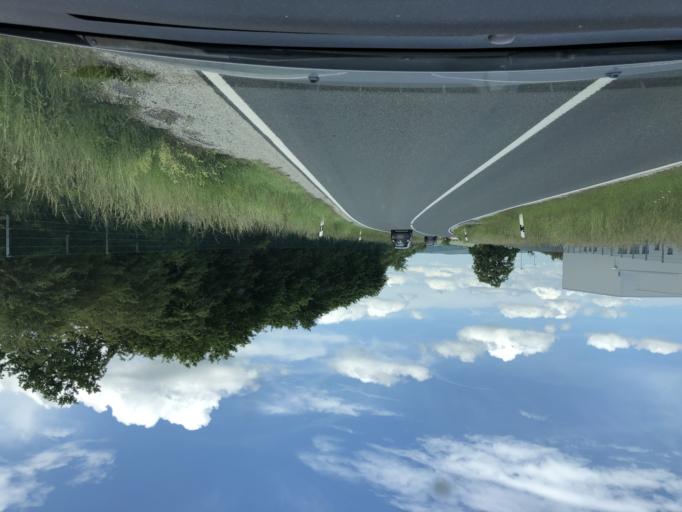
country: DE
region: Thuringia
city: Kefferhausen
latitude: 51.3023
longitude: 10.2896
